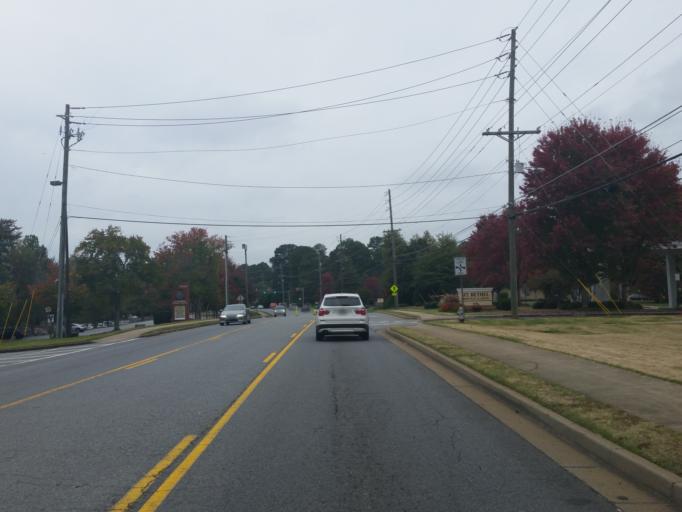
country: US
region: Georgia
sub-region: Fulton County
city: Sandy Springs
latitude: 33.9635
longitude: -84.4227
